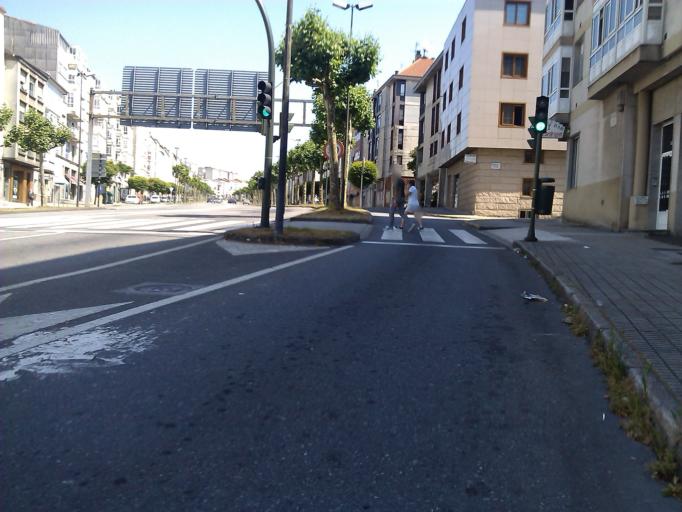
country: ES
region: Galicia
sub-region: Provincia da Coruna
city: Santiago de Compostela
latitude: 42.8795
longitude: -8.5329
